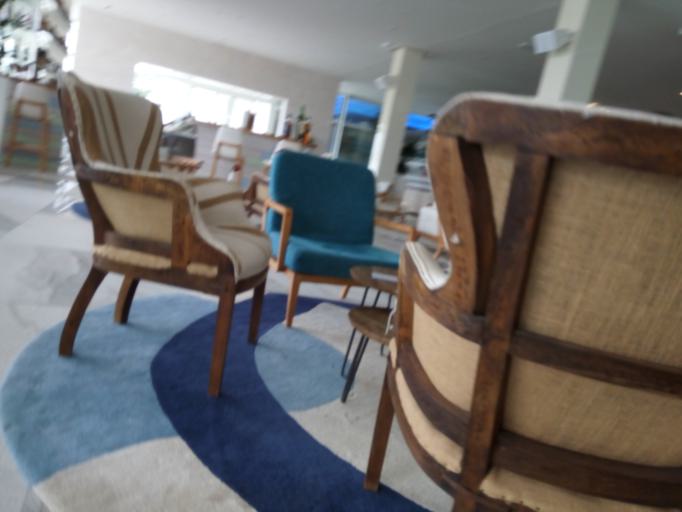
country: HR
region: Sibensko-Kniniska
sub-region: Grad Sibenik
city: Sibenik
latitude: 43.6959
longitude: 15.8844
